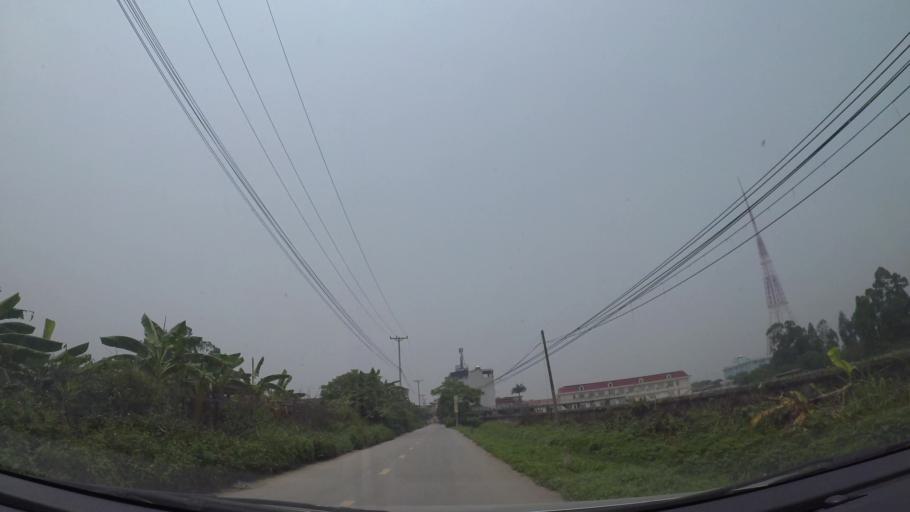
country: VN
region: Ha Noi
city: Ha Dong
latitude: 20.9979
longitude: 105.7660
